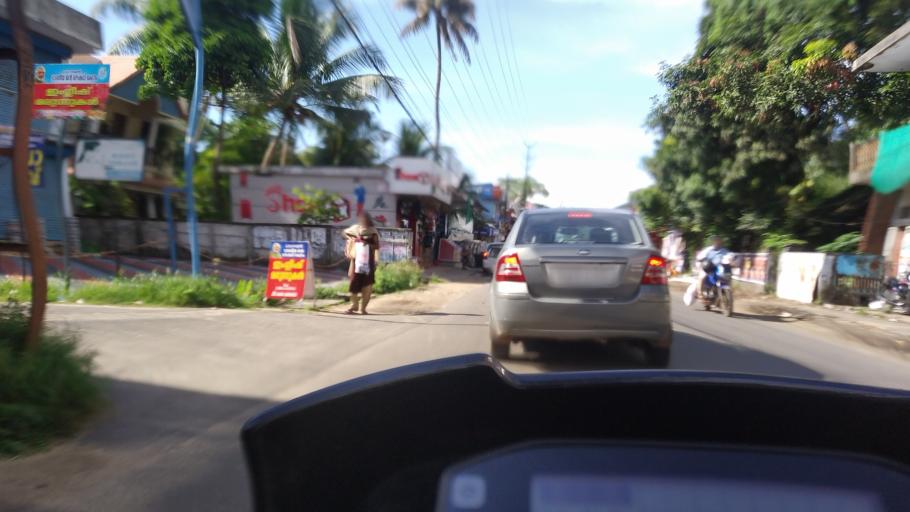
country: IN
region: Kerala
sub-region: Ernakulam
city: Elur
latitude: 10.0460
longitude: 76.2176
